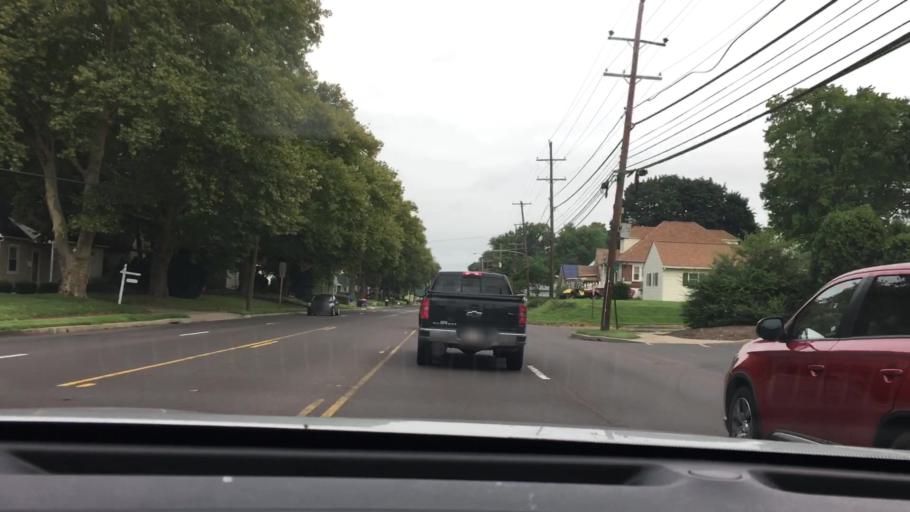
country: US
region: Pennsylvania
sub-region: Montgomery County
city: Hatboro
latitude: 40.1907
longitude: -75.1042
